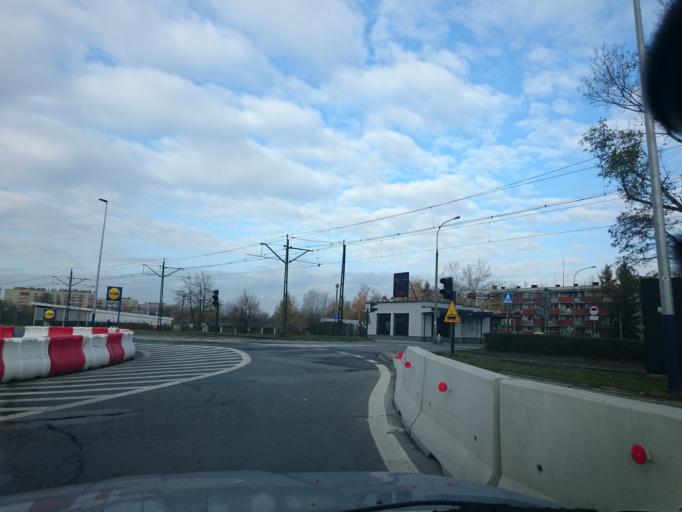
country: PL
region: Lesser Poland Voivodeship
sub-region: Powiat wielicki
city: Czarnochowice
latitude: 50.0166
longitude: 20.0166
